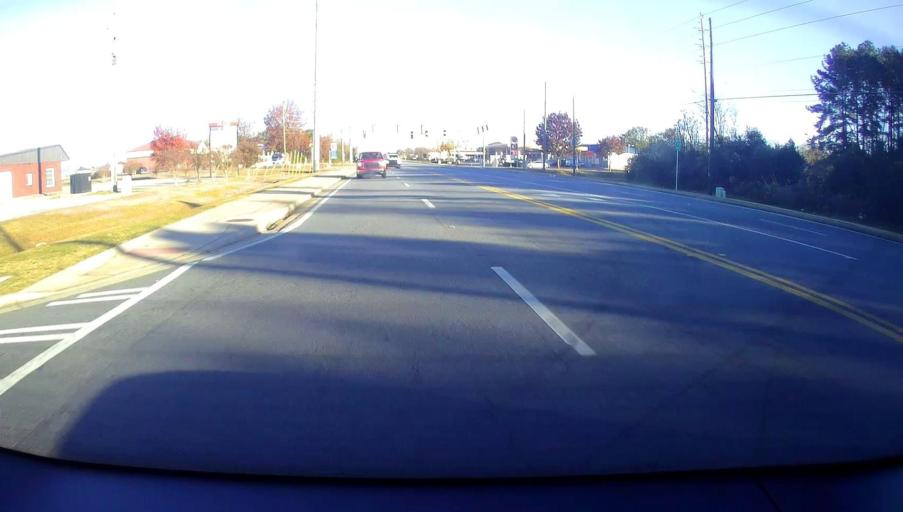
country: US
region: Georgia
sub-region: Houston County
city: Centerville
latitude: 32.6204
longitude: -83.7098
